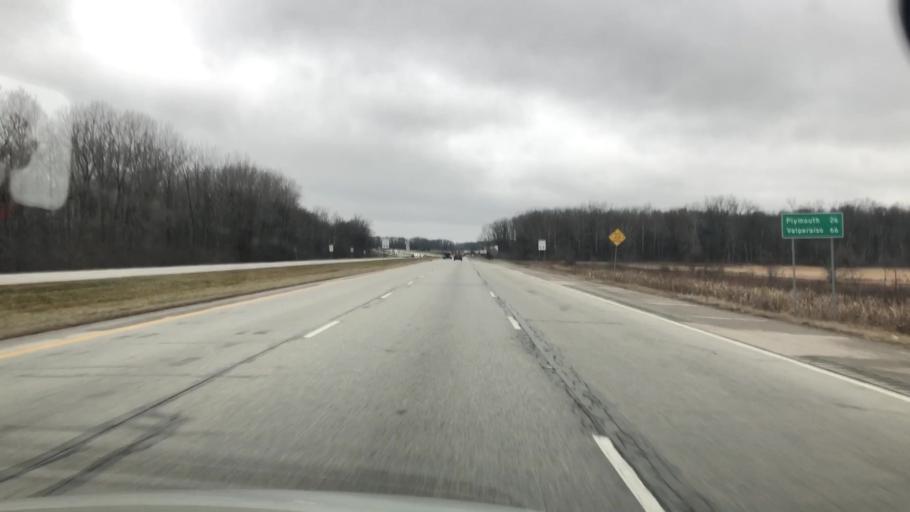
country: US
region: Indiana
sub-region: Kosciusko County
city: Warsaw
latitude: 41.2683
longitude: -85.8587
